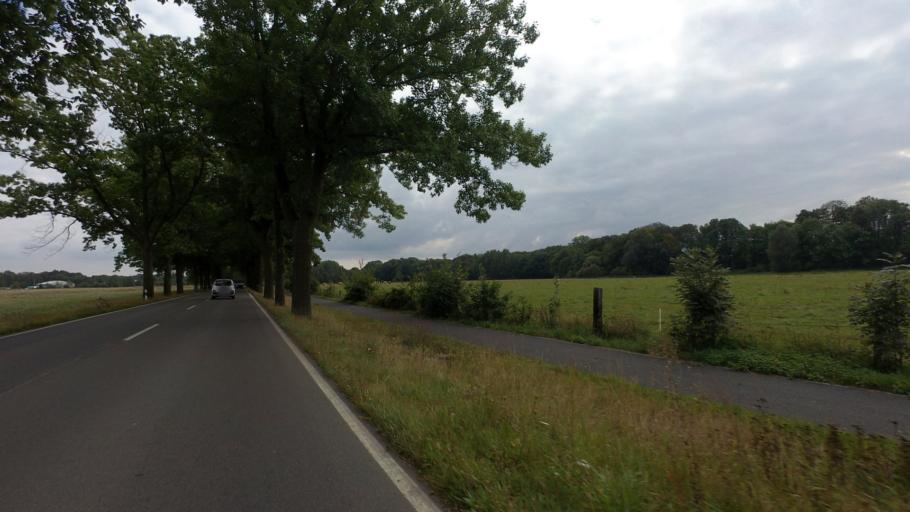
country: DE
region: Saxony
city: Konigswartha
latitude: 51.3583
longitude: 14.3183
